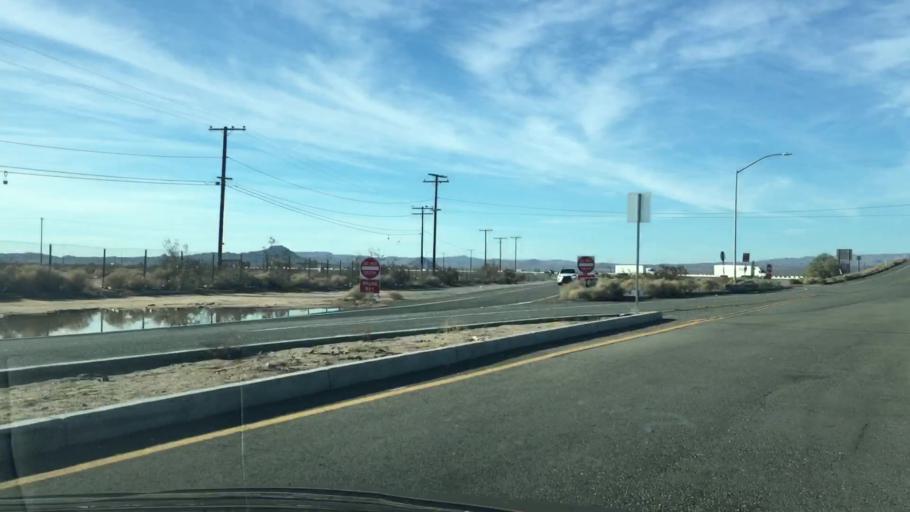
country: US
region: California
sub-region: San Bernardino County
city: Barstow
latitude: 34.9073
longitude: -116.8361
